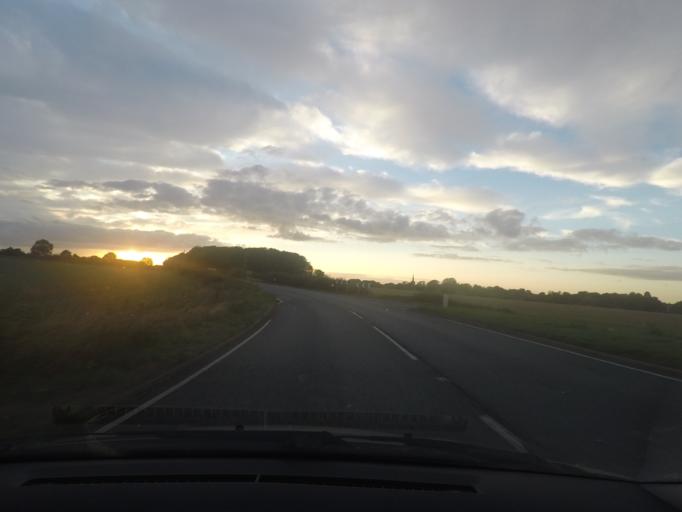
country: GB
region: England
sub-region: North Lincolnshire
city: Croxton
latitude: 53.5825
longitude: -0.3245
